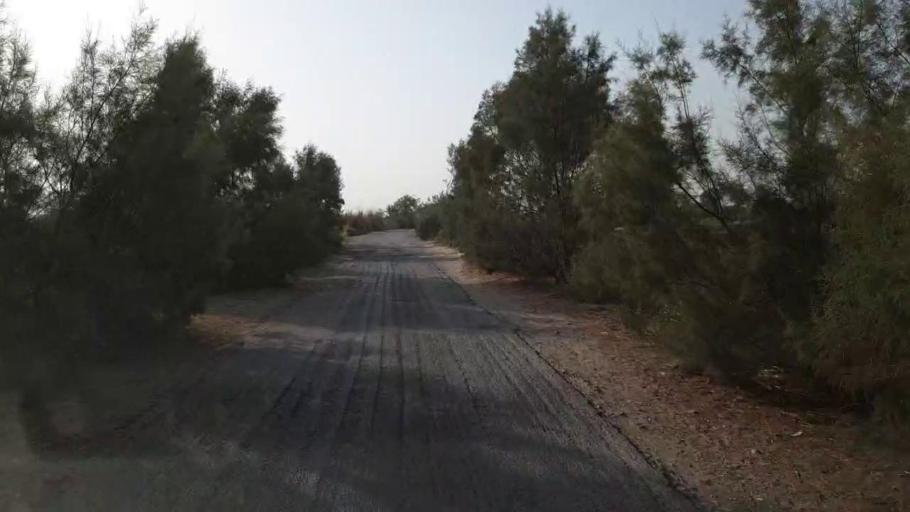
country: PK
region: Sindh
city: Jam Sahib
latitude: 26.4904
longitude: 68.8588
